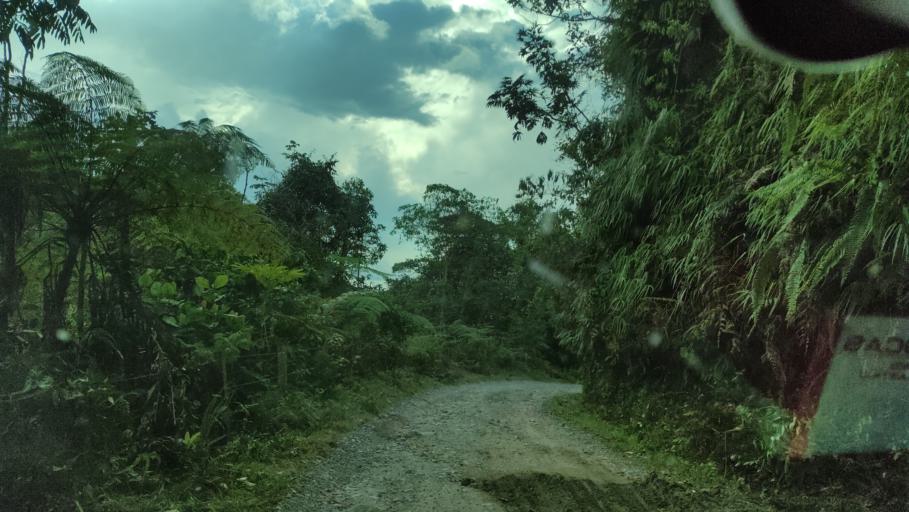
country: CO
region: Valle del Cauca
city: San Pedro
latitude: 3.8797
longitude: -76.1527
